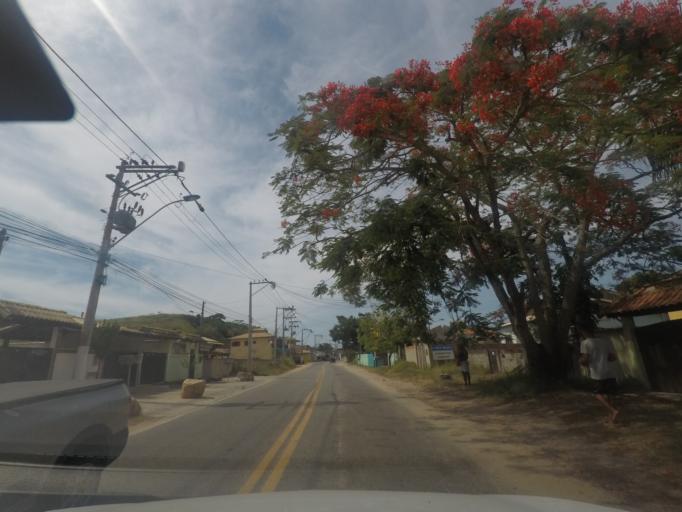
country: BR
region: Rio de Janeiro
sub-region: Marica
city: Marica
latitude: -22.9482
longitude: -42.6976
